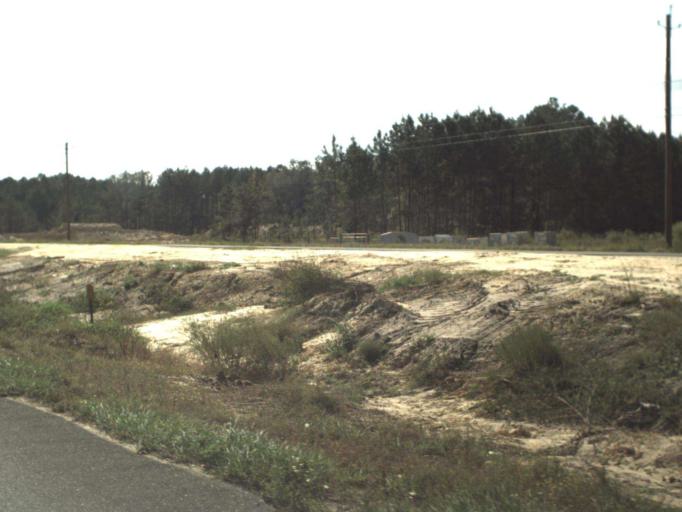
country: US
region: Florida
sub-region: Holmes County
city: Bonifay
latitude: 30.6465
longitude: -85.6996
